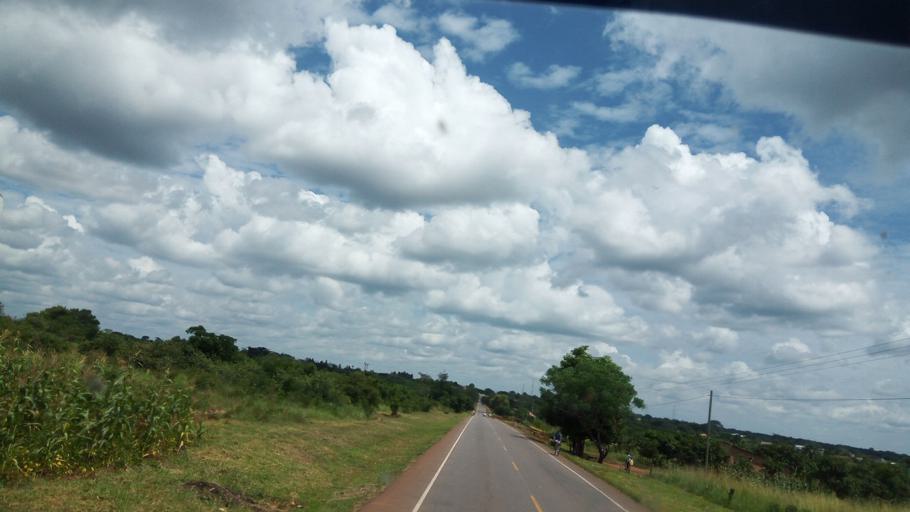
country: UG
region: Central Region
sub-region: Nakasongola District
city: Nakasongola
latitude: 1.4063
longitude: 32.2765
